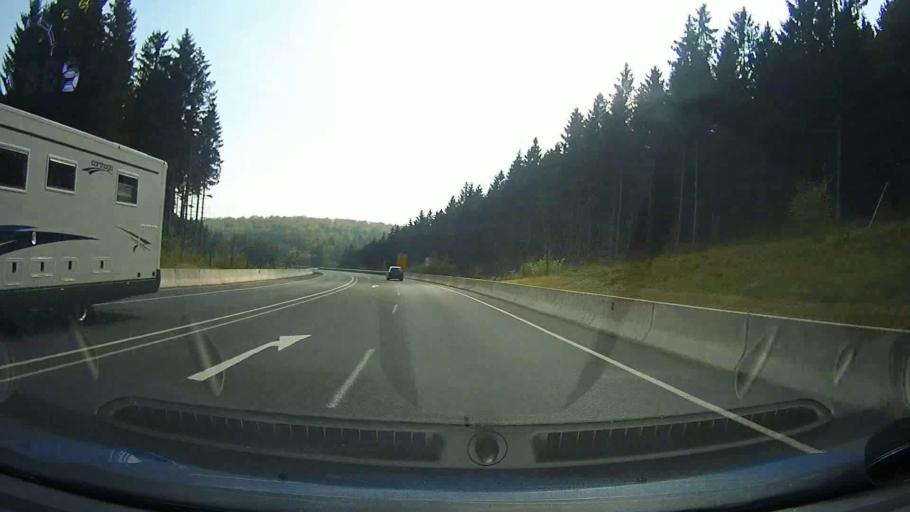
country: DE
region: Lower Saxony
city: Adelebsen
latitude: 51.6389
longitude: 9.7639
